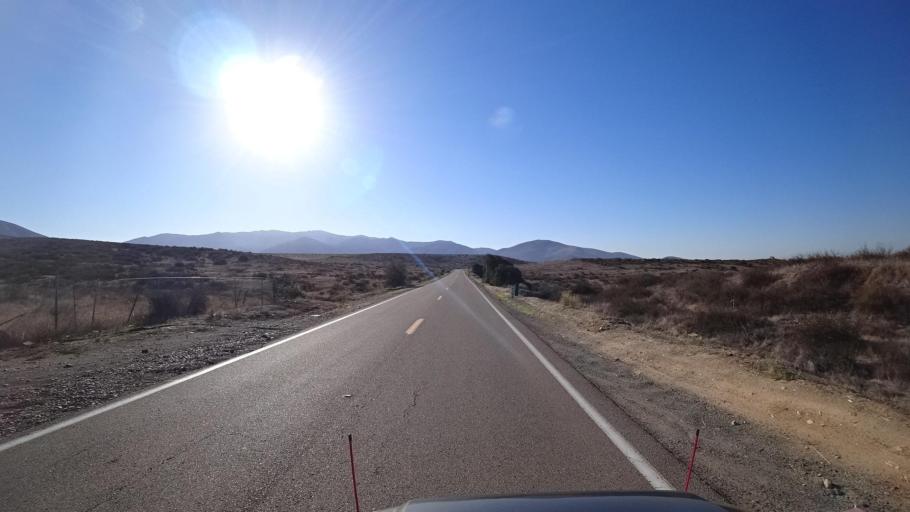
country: US
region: California
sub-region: San Diego County
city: Jamul
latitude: 32.6432
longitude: -116.9254
